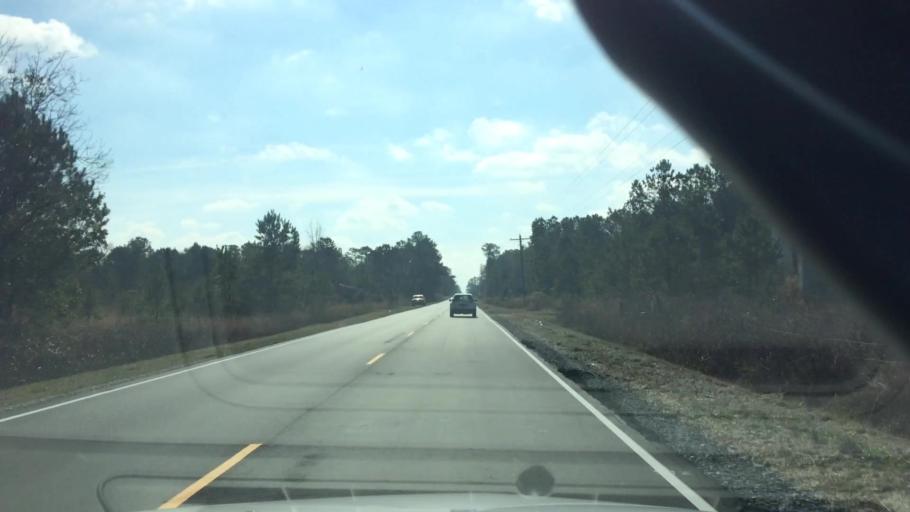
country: US
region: North Carolina
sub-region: Duplin County
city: Beulaville
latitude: 34.9878
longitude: -77.7582
